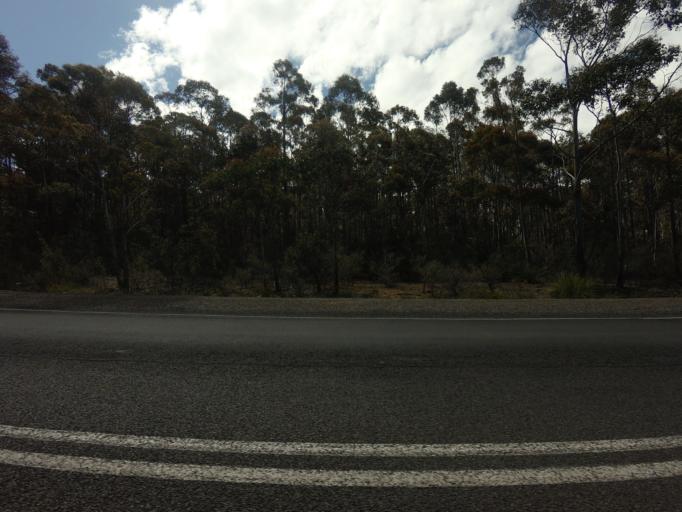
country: AU
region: Tasmania
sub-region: Break O'Day
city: St Helens
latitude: -42.0090
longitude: 147.8884
